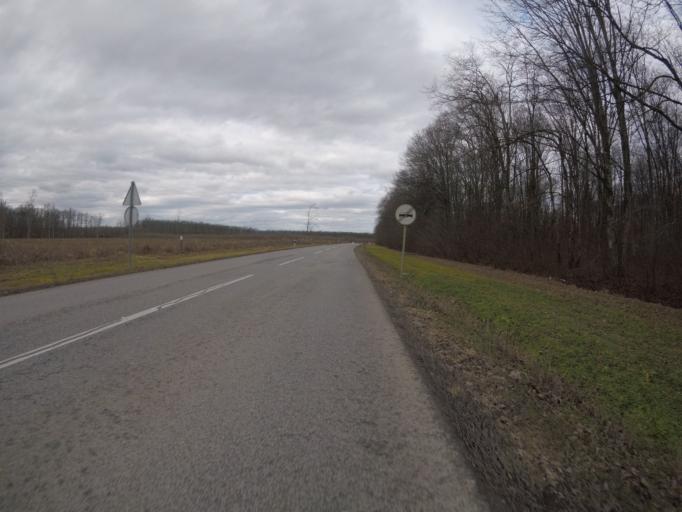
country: HR
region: Zagrebacka
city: Gradici
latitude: 45.6570
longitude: 16.0530
